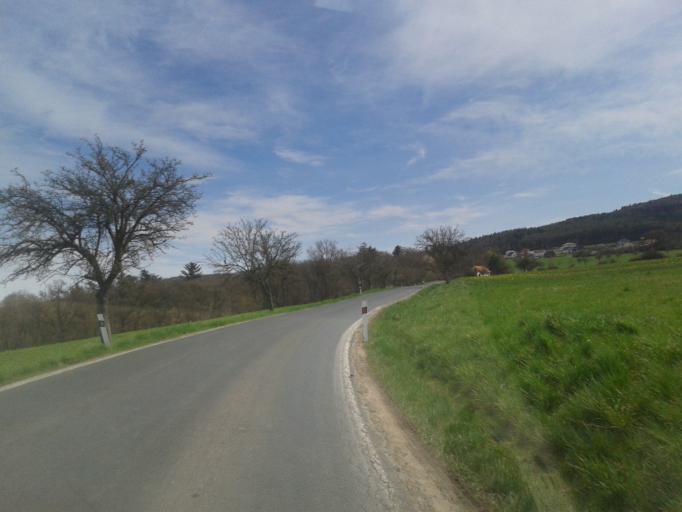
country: CZ
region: Central Bohemia
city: Revnice
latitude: 49.8941
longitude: 14.2003
